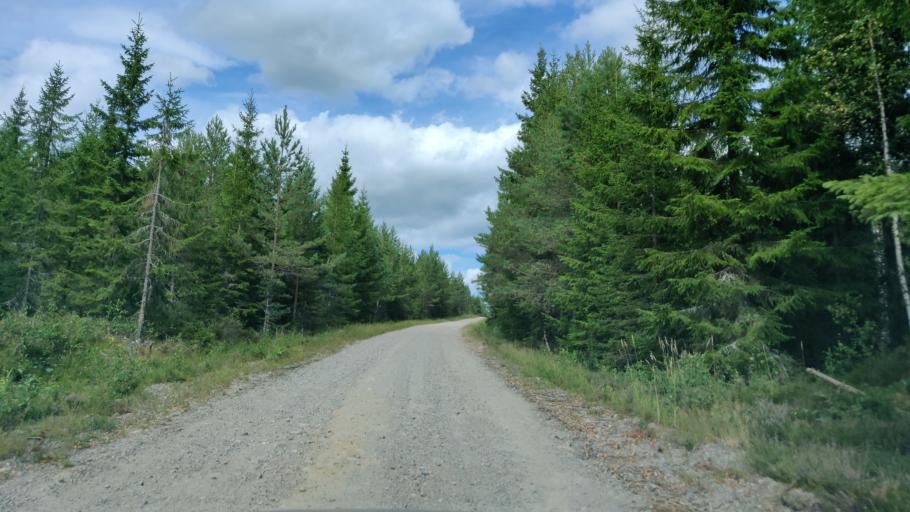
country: SE
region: Vaermland
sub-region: Hagfors Kommun
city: Hagfors
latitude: 60.0109
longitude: 13.7276
